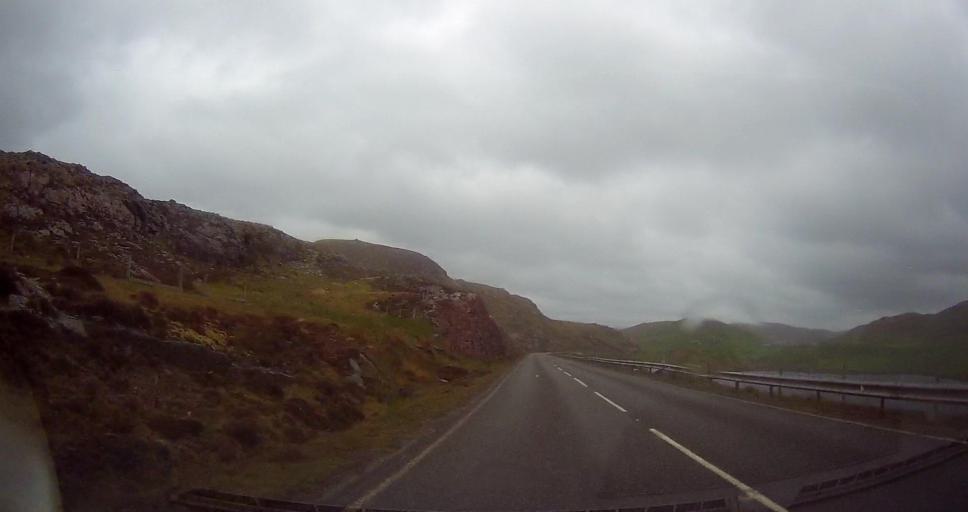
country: GB
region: Scotland
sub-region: Shetland Islands
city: Lerwick
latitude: 60.4143
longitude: -1.3927
